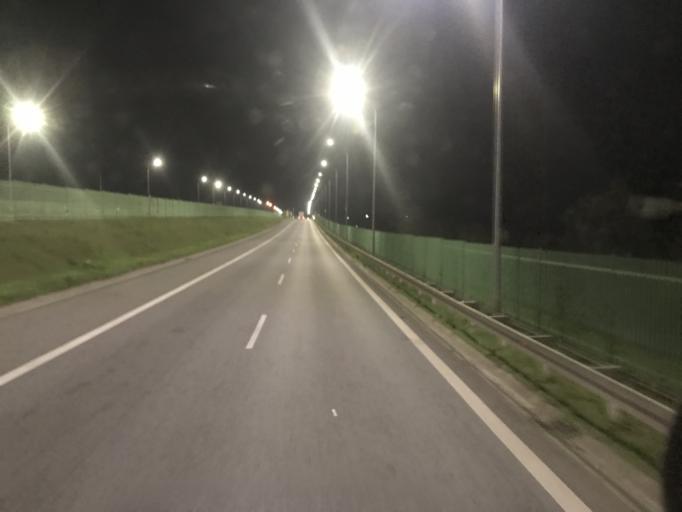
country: PL
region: Lublin Voivodeship
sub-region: Powiat bialski
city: Terespol
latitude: 52.1120
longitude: 23.5626
